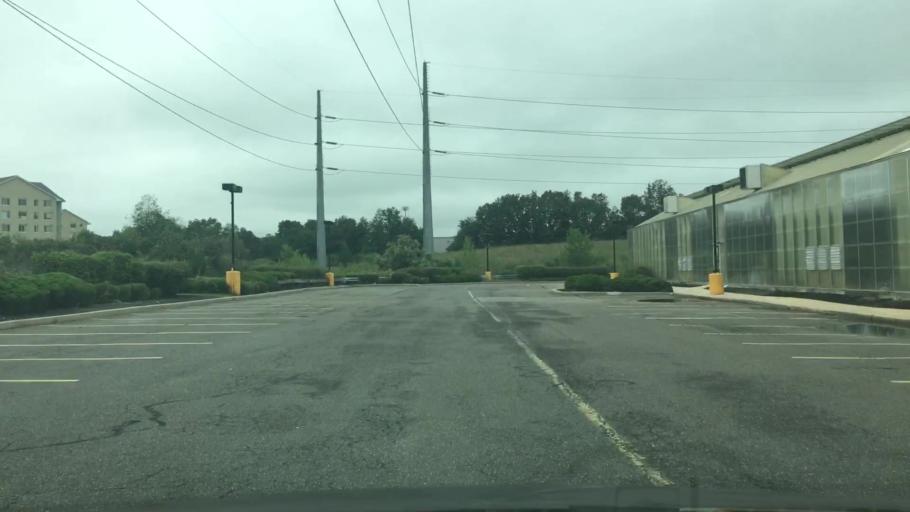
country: US
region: Massachusetts
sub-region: Essex County
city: Danvers
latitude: 42.5536
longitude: -70.9681
